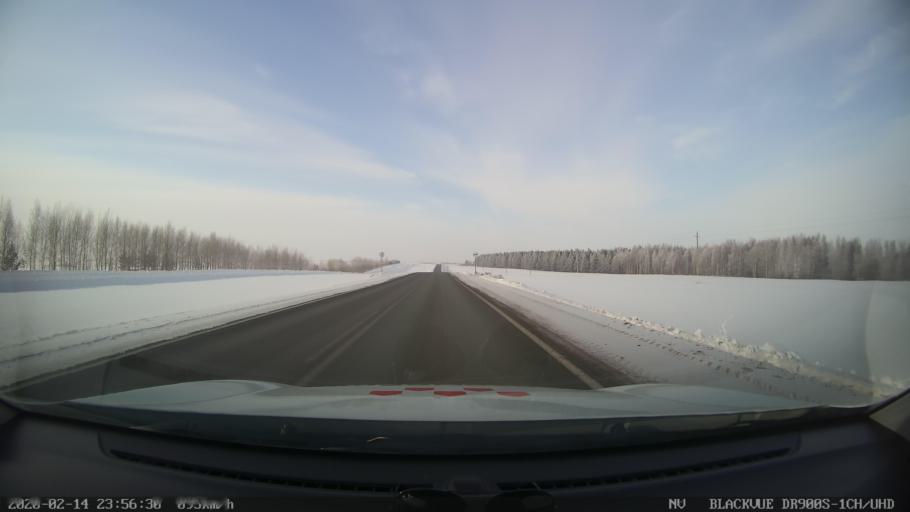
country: RU
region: Tatarstan
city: Kuybyshevskiy Zaton
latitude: 55.3253
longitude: 49.1289
